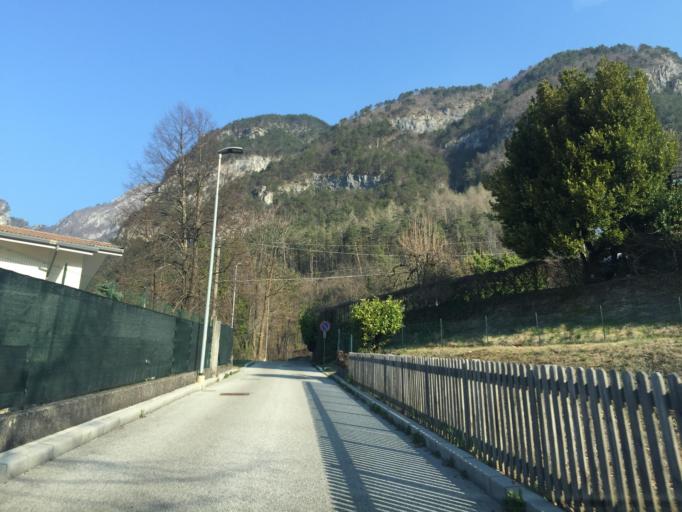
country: IT
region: Friuli Venezia Giulia
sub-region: Provincia di Udine
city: Amaro
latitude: 46.3761
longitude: 13.0976
